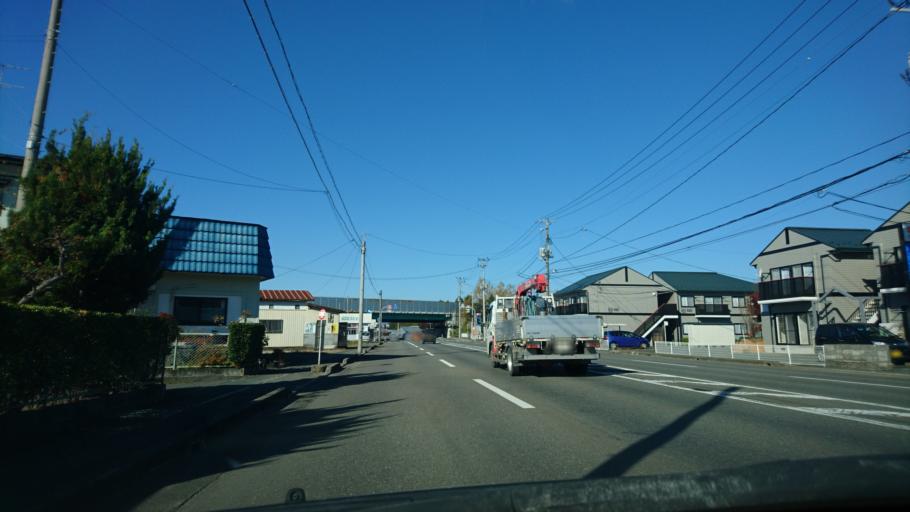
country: JP
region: Iwate
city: Mizusawa
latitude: 39.1438
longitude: 141.1217
